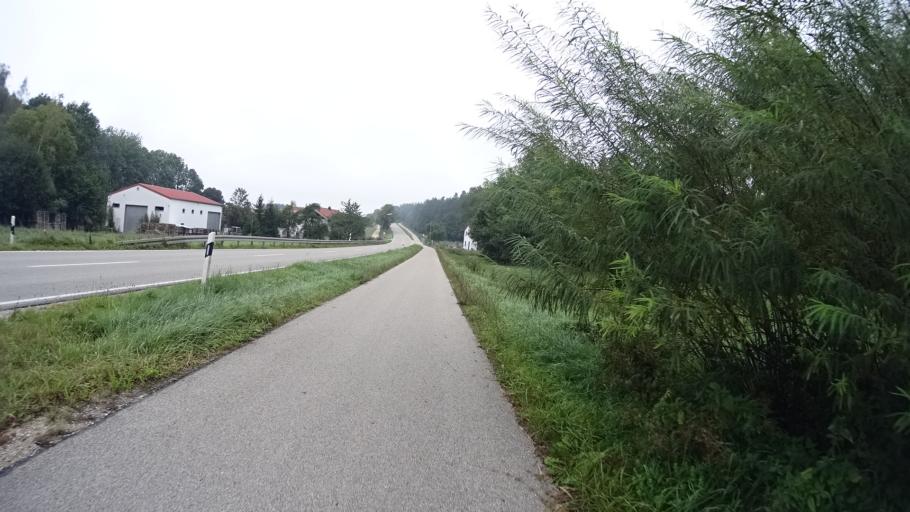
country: DE
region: Bavaria
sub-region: Upper Bavaria
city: Denkendorf
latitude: 48.9110
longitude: 11.4565
